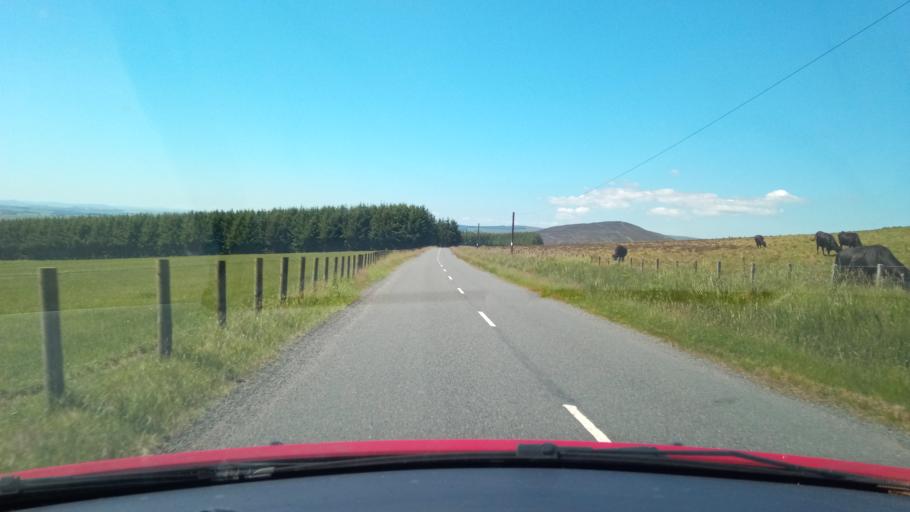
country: GB
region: Scotland
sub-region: The Scottish Borders
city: Duns
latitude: 55.7813
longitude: -2.4304
